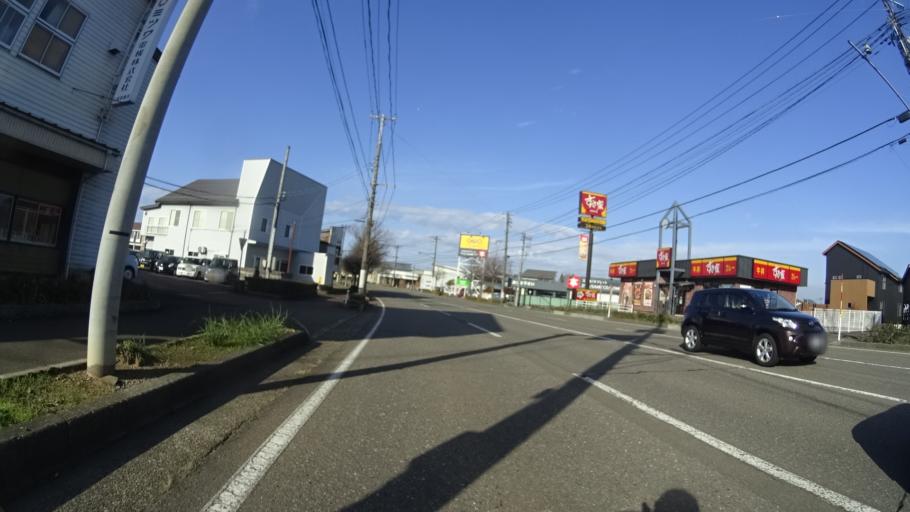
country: JP
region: Niigata
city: Joetsu
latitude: 37.1215
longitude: 138.2520
